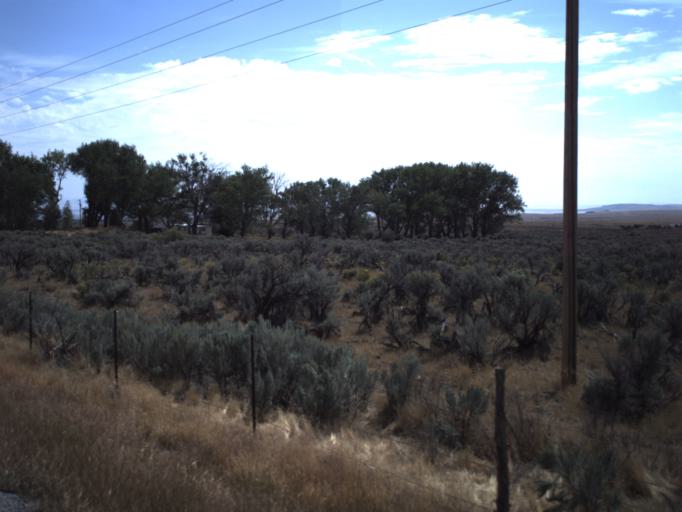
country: US
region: Idaho
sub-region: Cassia County
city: Burley
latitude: 41.8172
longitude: -113.2801
